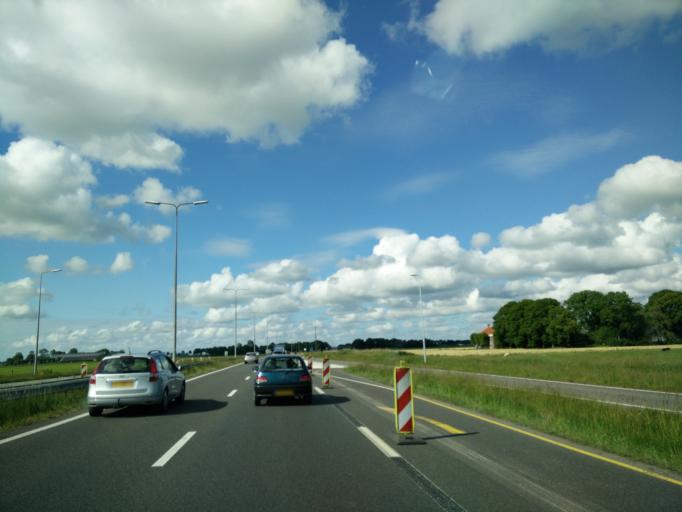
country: NL
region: Groningen
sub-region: Gemeente Groningen
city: Korrewegwijk
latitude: 53.2529
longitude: 6.5751
